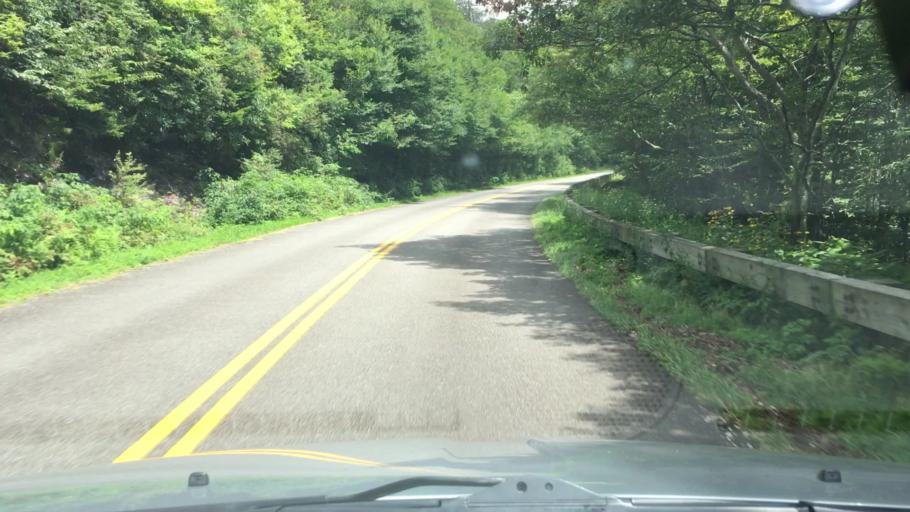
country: US
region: North Carolina
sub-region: Buncombe County
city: Black Mountain
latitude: 35.7210
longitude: -82.2823
